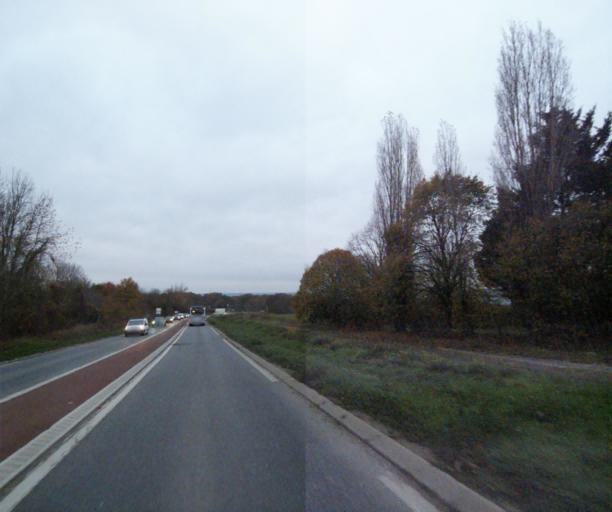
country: FR
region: Ile-de-France
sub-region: Departement des Yvelines
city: Medan
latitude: 48.9558
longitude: 1.9804
